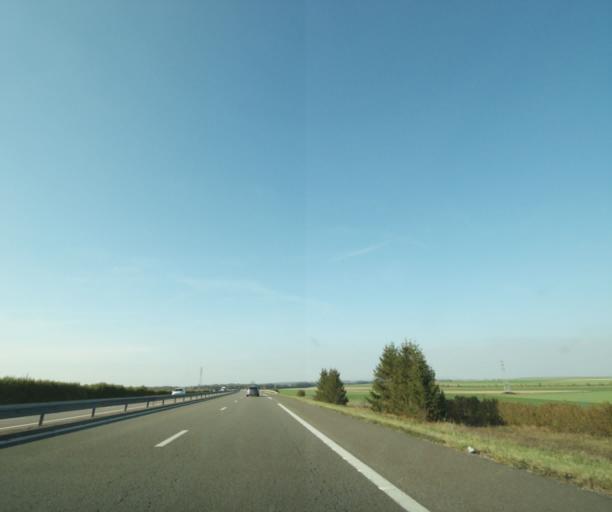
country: FR
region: Champagne-Ardenne
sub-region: Departement de la Marne
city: Saint-Memmie
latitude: 49.0367
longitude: 4.4286
